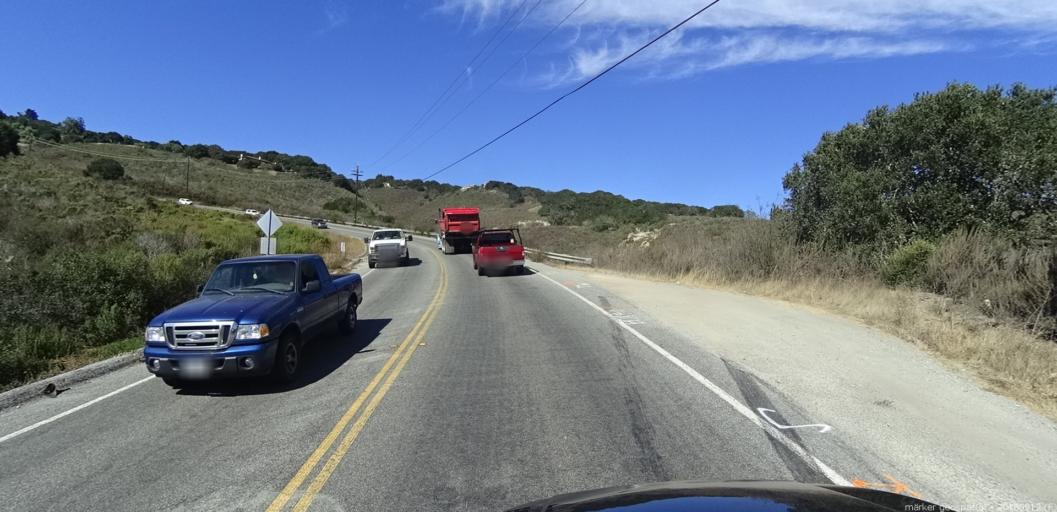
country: US
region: California
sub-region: Monterey County
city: Carmel Valley Village
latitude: 36.5553
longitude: -121.7559
